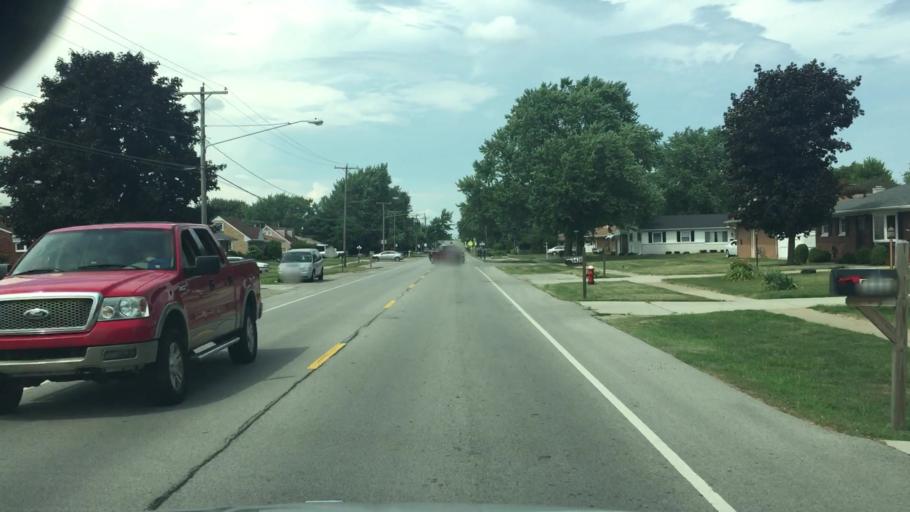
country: US
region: Ohio
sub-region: Lucas County
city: Oregon
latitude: 41.7168
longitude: -83.4982
